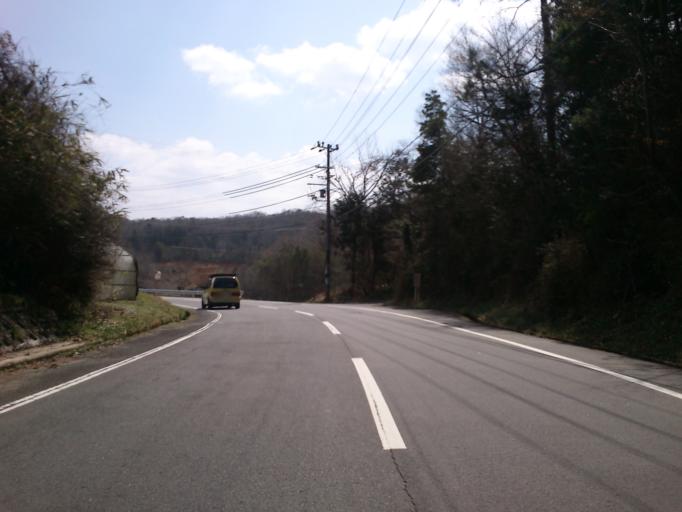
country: JP
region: Mie
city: Ueno-ebisumachi
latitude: 34.7272
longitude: 136.0226
